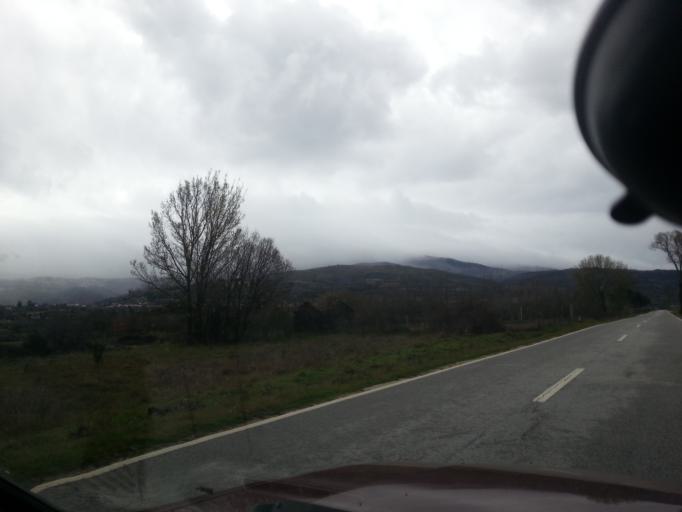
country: PT
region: Guarda
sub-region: Fornos de Algodres
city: Fornos de Algodres
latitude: 40.5416
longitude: -7.5695
